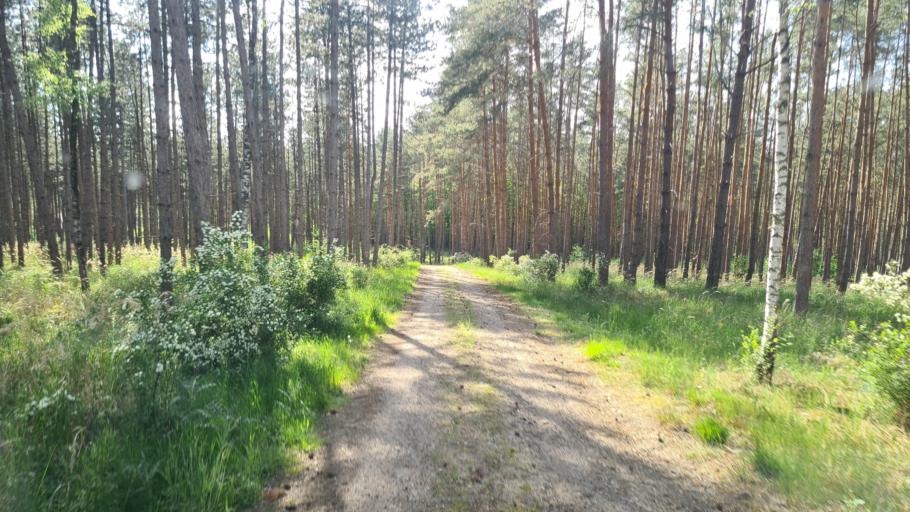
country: DE
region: Brandenburg
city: Schonborn
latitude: 51.5810
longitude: 13.4700
